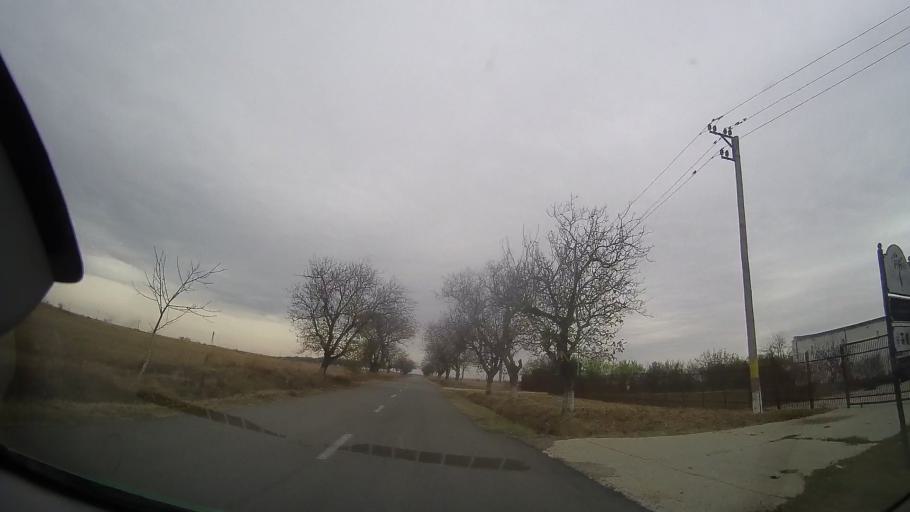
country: RO
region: Prahova
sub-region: Comuna Vadu Sapat
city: Vadu Sapat
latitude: 45.0222
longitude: 26.3921
